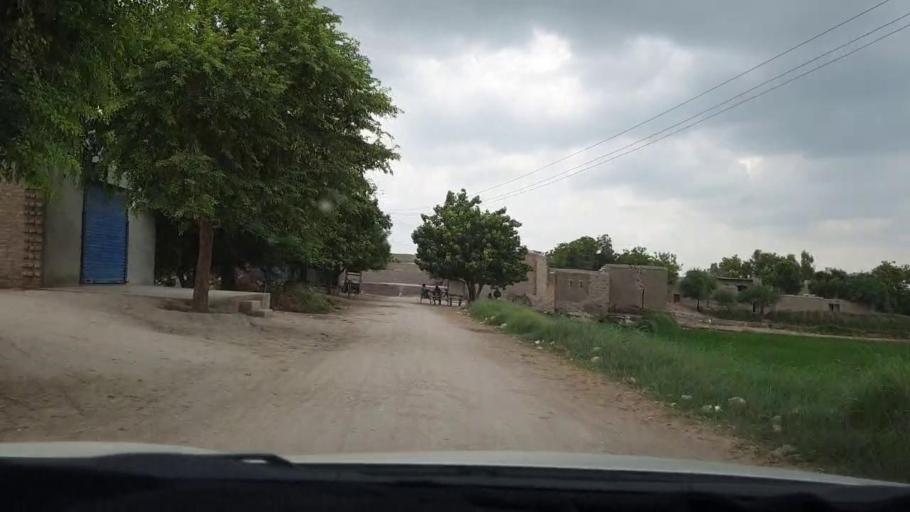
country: PK
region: Sindh
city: Dokri
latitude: 27.3264
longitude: 68.1035
